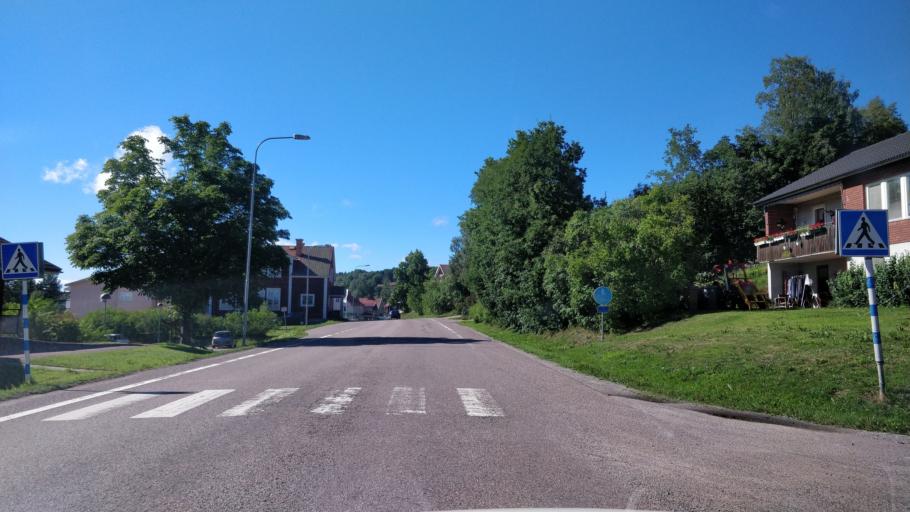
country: SE
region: Dalarna
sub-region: Faluns Kommun
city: Bjursas
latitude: 60.7384
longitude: 15.4471
